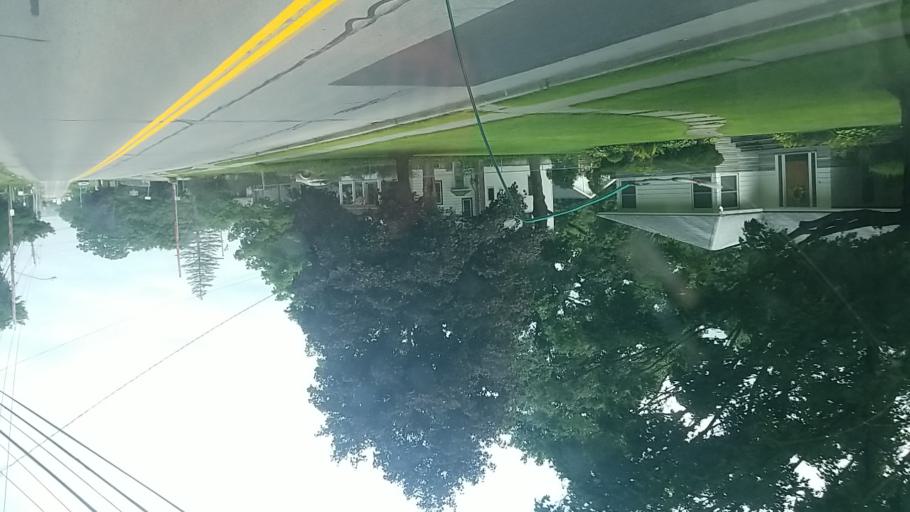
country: US
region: New York
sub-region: Montgomery County
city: Canajoharie
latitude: 42.9129
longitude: -74.5807
